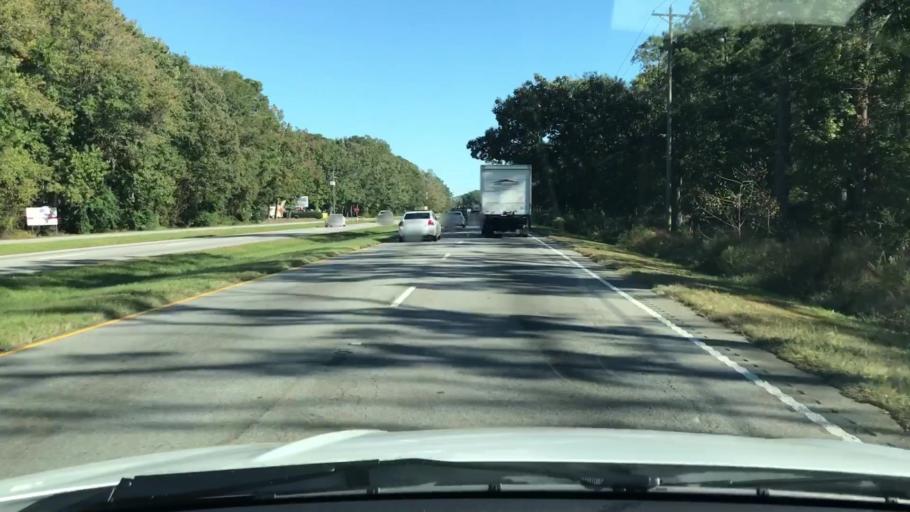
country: US
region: South Carolina
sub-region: Charleston County
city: Shell Point
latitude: 32.7986
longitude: -80.0899
